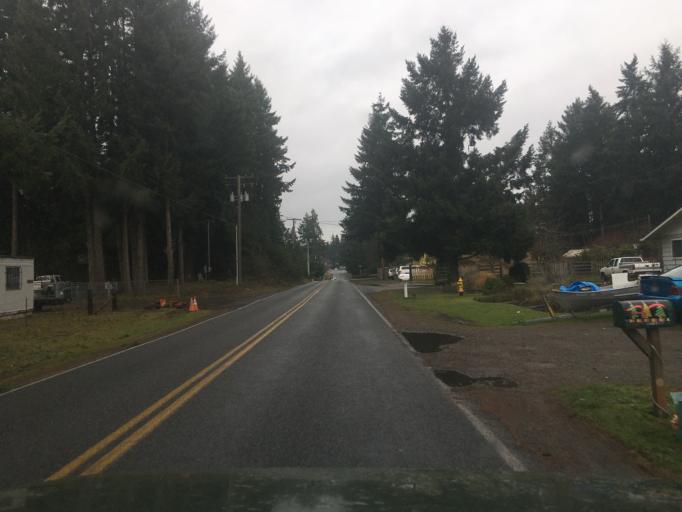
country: US
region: Washington
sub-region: Thurston County
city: Tanglewilde-Thompson Place
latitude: 47.0471
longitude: -122.7913
